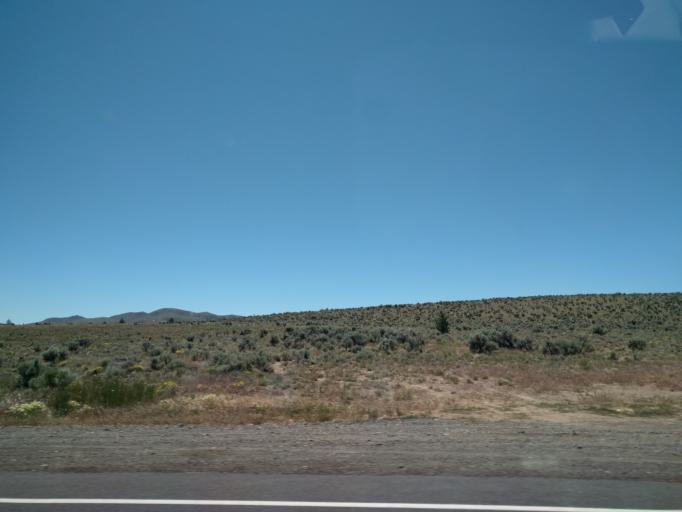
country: US
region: Oregon
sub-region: Harney County
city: Hines
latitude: 43.5797
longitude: -119.9483
